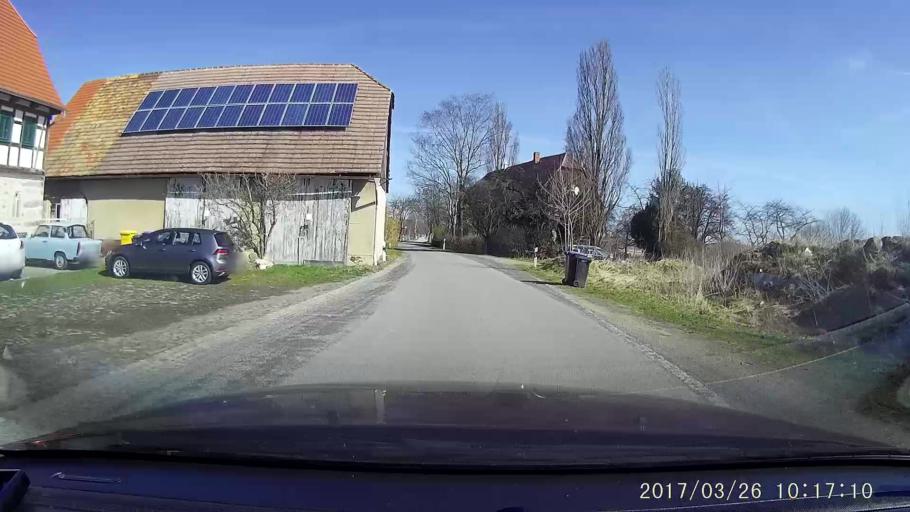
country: DE
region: Saxony
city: Herrnhut
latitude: 51.0627
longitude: 14.7602
